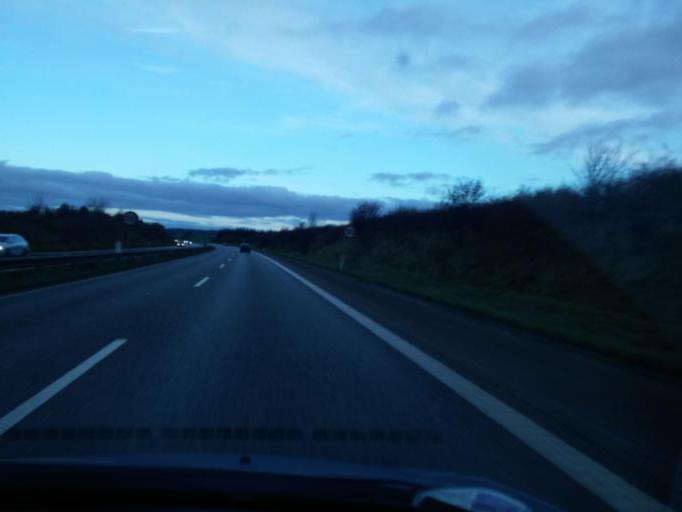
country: DK
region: South Denmark
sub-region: Fredericia Kommune
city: Taulov
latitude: 55.5834
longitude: 9.6103
